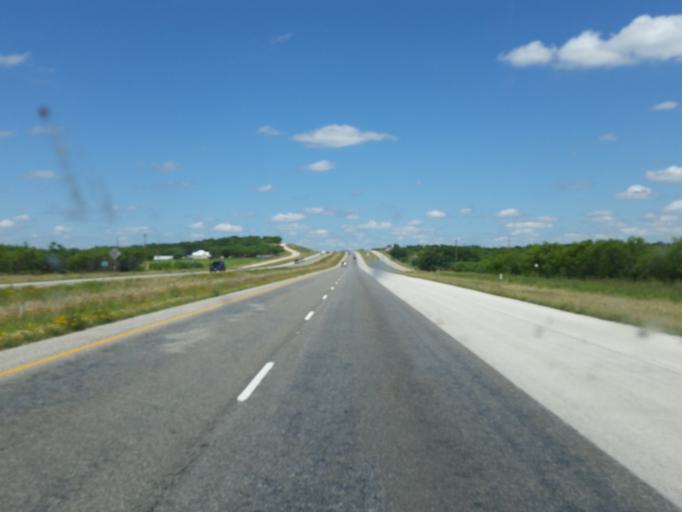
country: US
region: Texas
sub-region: Eastland County
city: Cisco
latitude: 32.3761
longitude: -99.0986
